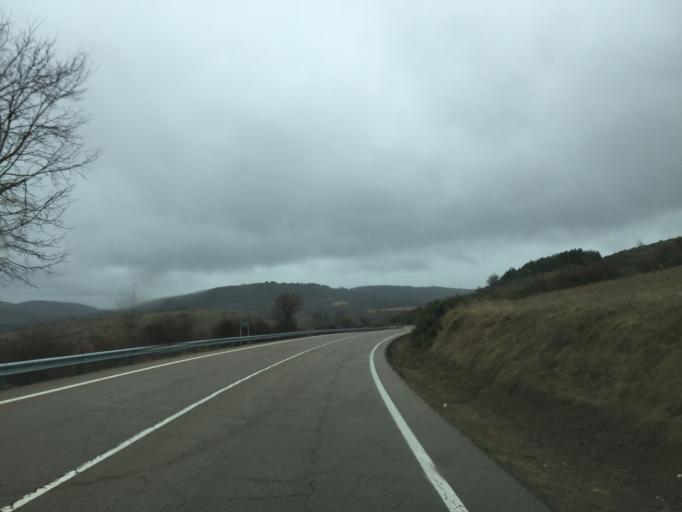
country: ES
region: Castille and Leon
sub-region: Provincia de Leon
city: Carrocera
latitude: 42.7845
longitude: -5.7489
